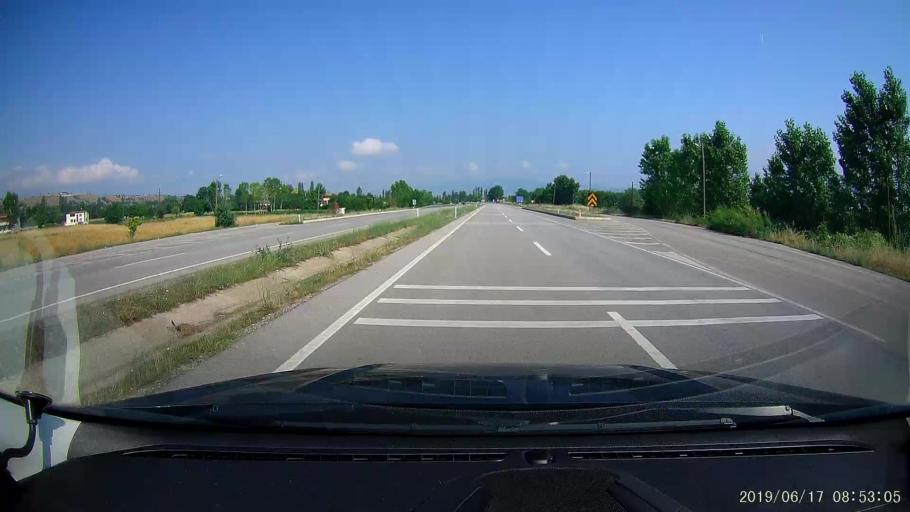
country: TR
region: Tokat
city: Erbaa
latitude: 40.7061
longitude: 36.4867
